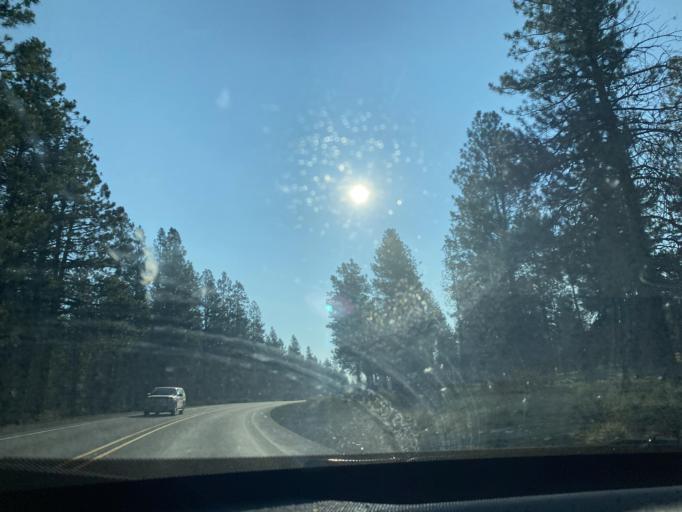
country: US
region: Oregon
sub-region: Deschutes County
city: Sunriver
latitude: 43.8703
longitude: -121.4113
